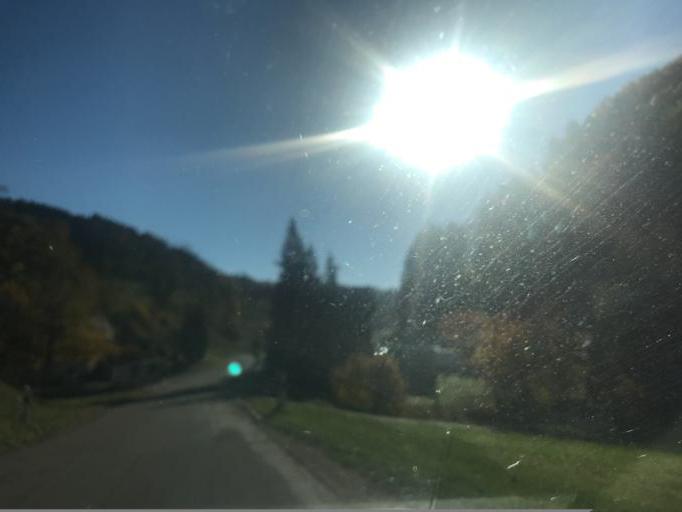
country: DE
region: Baden-Wuerttemberg
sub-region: Freiburg Region
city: Sexau
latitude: 48.1425
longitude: 7.9326
